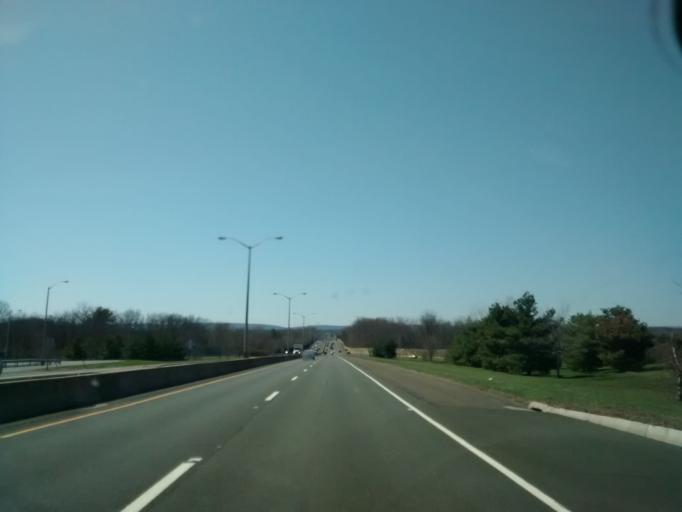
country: US
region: Connecticut
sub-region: Hartford County
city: South Windsor
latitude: 41.8056
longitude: -72.6148
